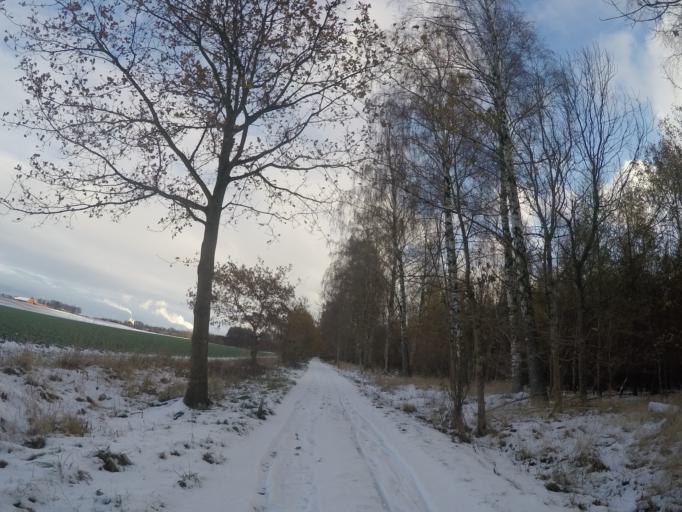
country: SE
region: Skane
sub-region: Lunds Kommun
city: Lund
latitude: 55.7864
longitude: 13.2183
